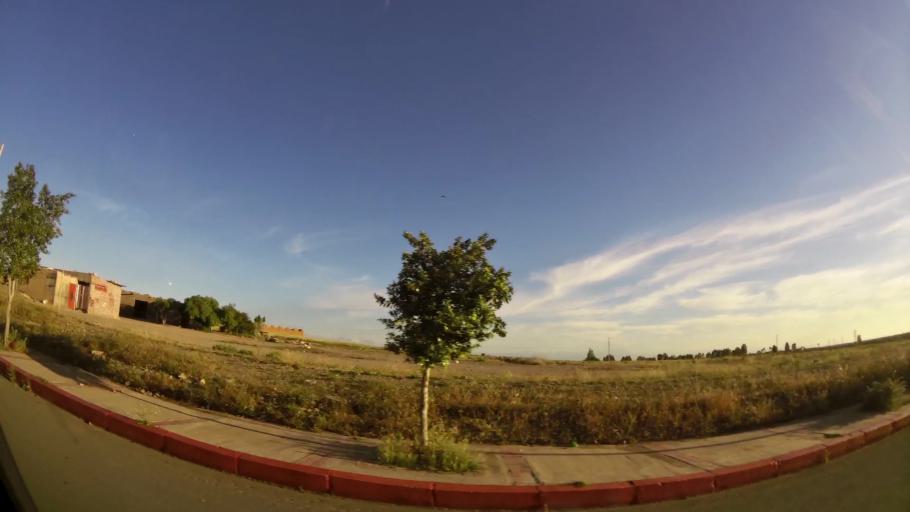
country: MA
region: Marrakech-Tensift-Al Haouz
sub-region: Marrakech
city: Marrakesh
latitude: 31.7426
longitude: -8.1103
